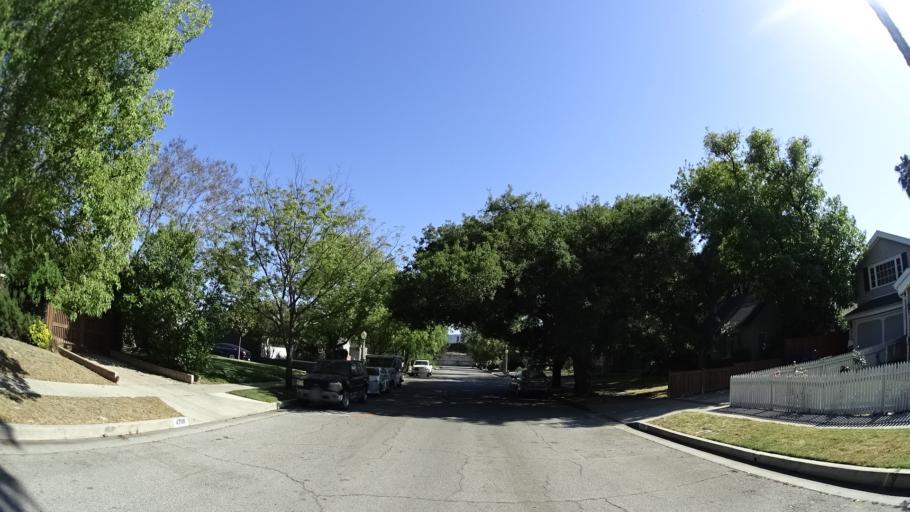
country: US
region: California
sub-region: Los Angeles County
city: North Hollywood
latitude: 34.1564
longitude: -118.3812
